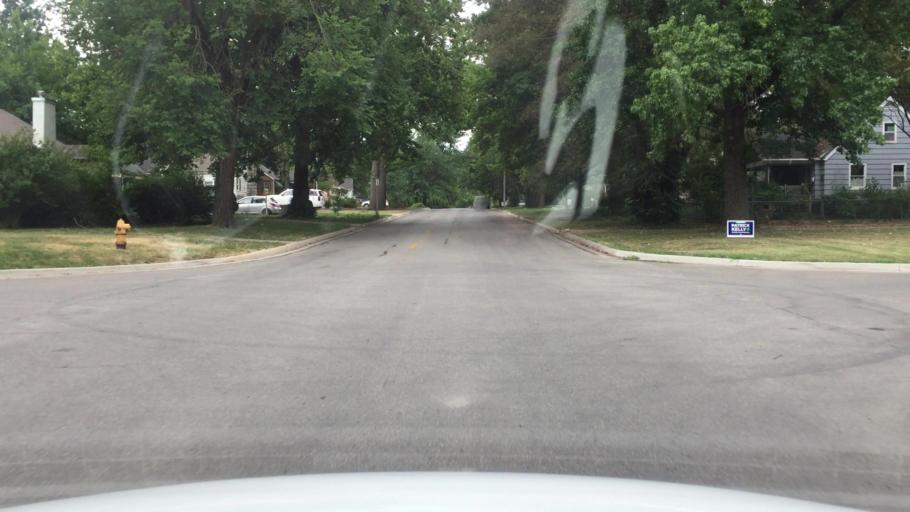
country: US
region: Kansas
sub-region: Douglas County
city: Lawrence
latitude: 38.9448
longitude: -95.2394
